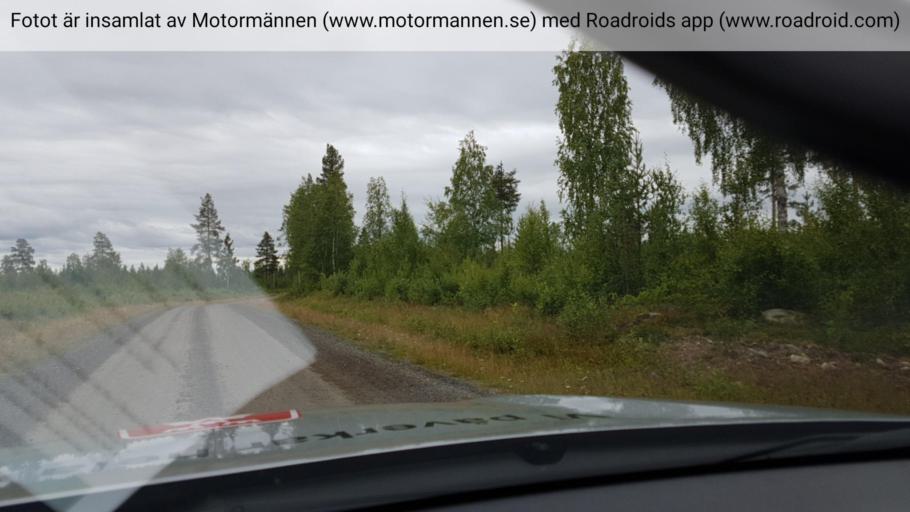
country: SE
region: Norrbotten
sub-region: Pajala Kommun
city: Pajala
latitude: 67.0473
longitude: 22.8412
